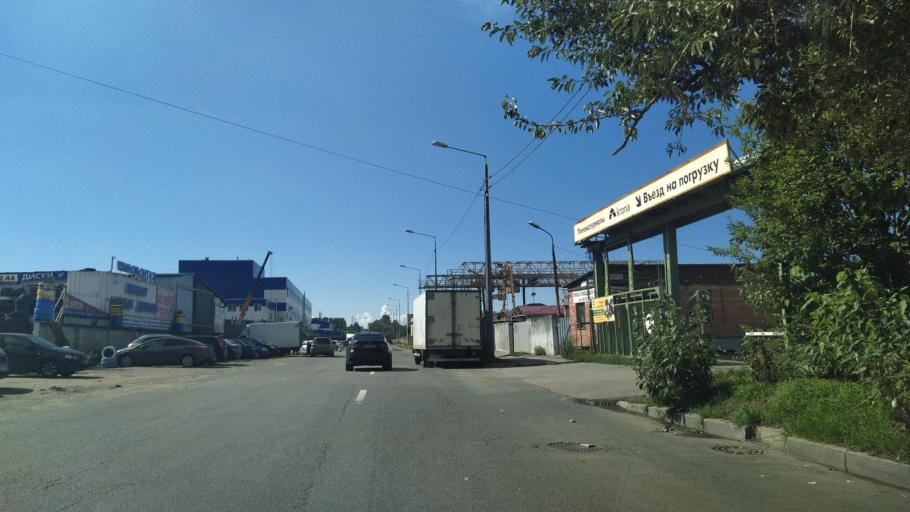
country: RU
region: Leningrad
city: Finlyandskiy
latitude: 59.9766
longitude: 30.3625
